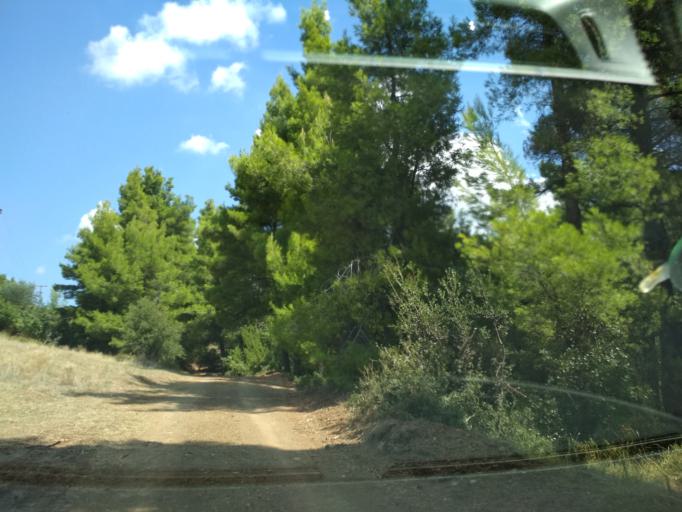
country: GR
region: Central Greece
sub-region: Nomos Evvoias
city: Roviai
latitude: 38.8361
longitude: 23.2783
